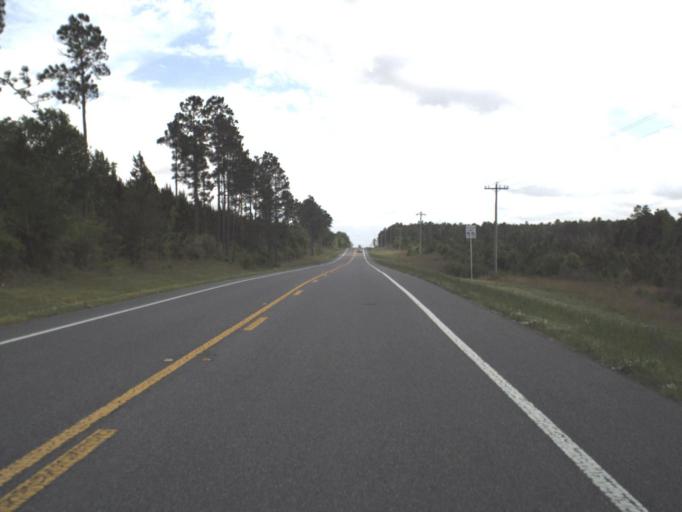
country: US
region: Florida
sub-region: Santa Rosa County
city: Wallace
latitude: 30.8352
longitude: -87.1415
